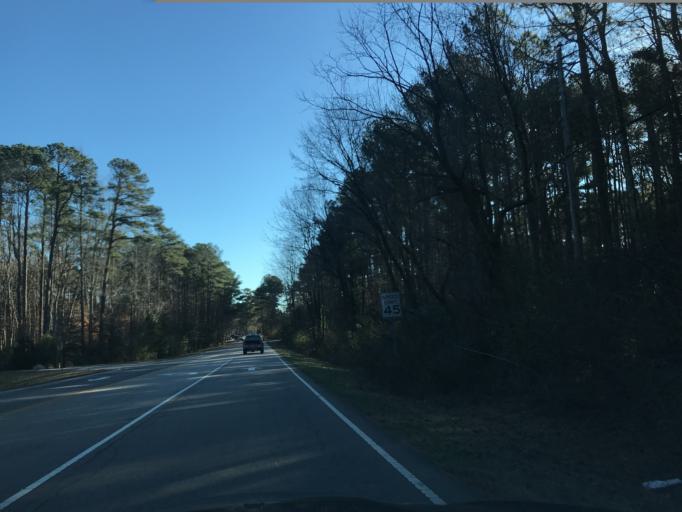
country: US
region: North Carolina
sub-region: Wake County
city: West Raleigh
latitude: 35.9078
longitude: -78.7152
